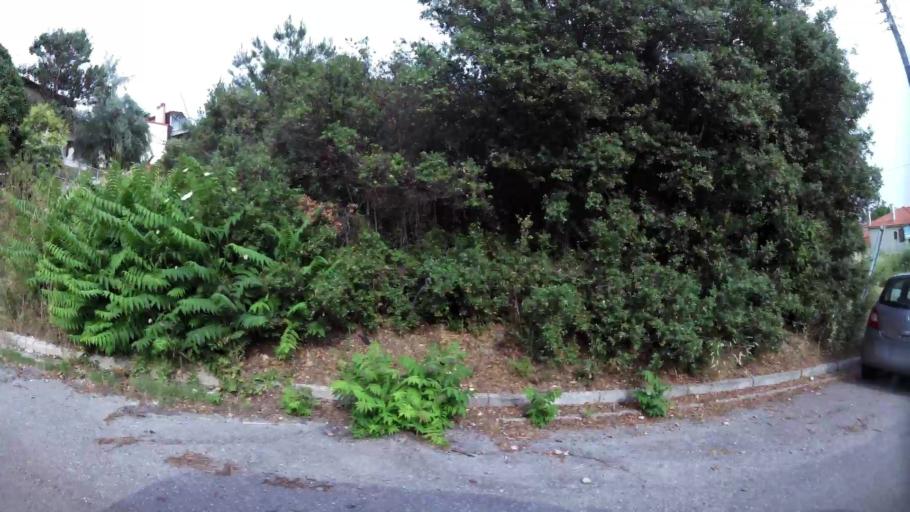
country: GR
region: Central Macedonia
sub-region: Nomos Thessalonikis
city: Oraiokastro
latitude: 40.7322
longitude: 22.9112
